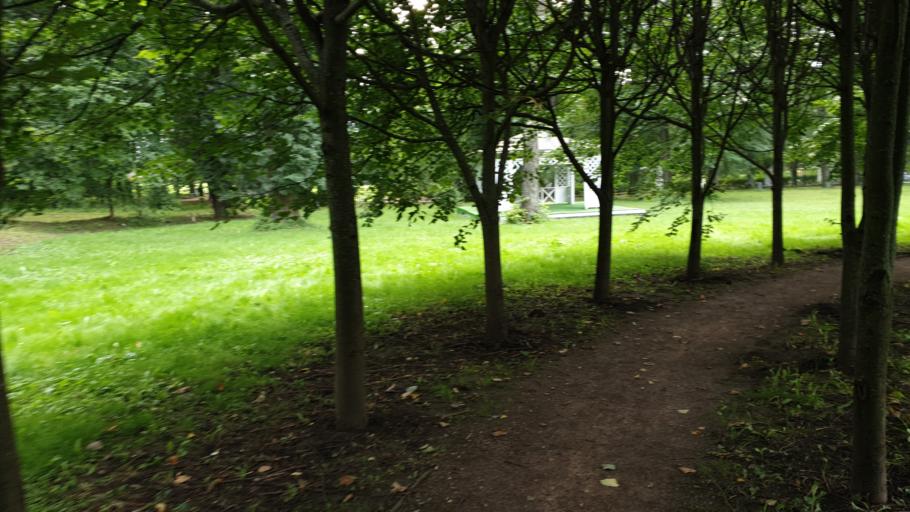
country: RU
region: Moskovskaya
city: Gorki-Leninskiye
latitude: 55.5043
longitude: 37.7659
